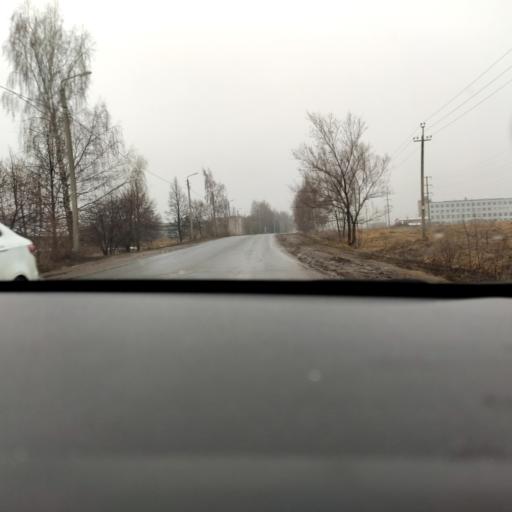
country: RU
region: Tatarstan
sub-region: Chistopol'skiy Rayon
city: Chistopol'
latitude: 55.3540
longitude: 50.6725
